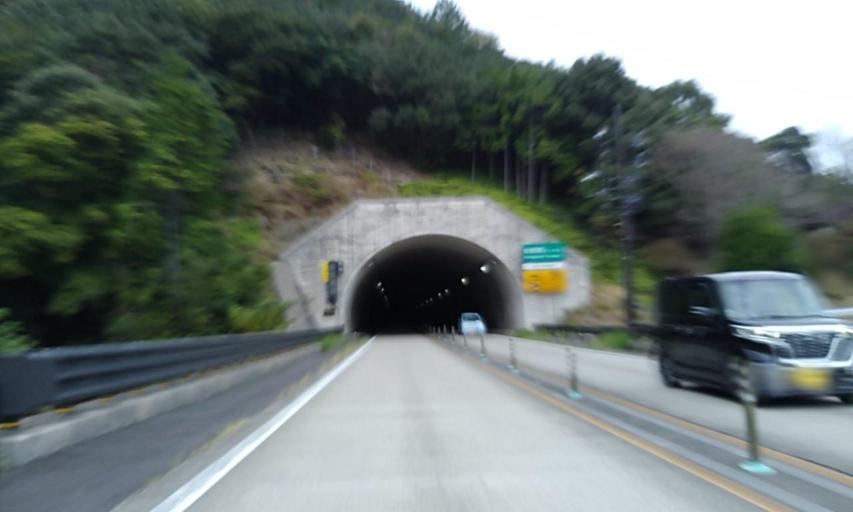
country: JP
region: Wakayama
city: Shingu
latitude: 33.6005
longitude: 135.9160
